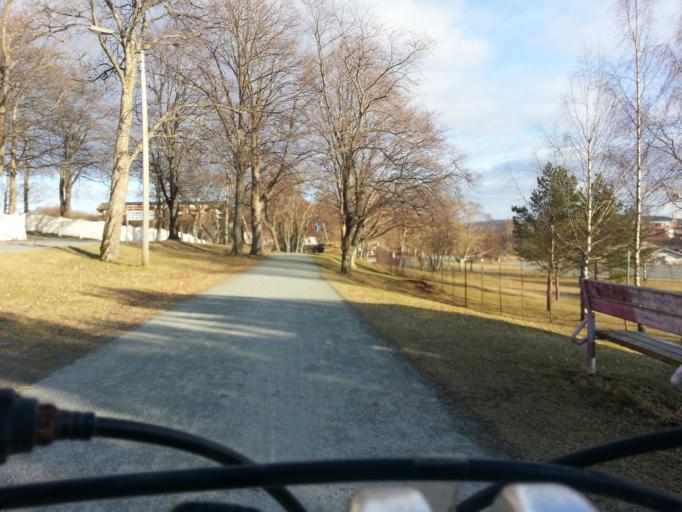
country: NO
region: Sor-Trondelag
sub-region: Trondheim
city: Trondheim
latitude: 63.4464
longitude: 10.4526
